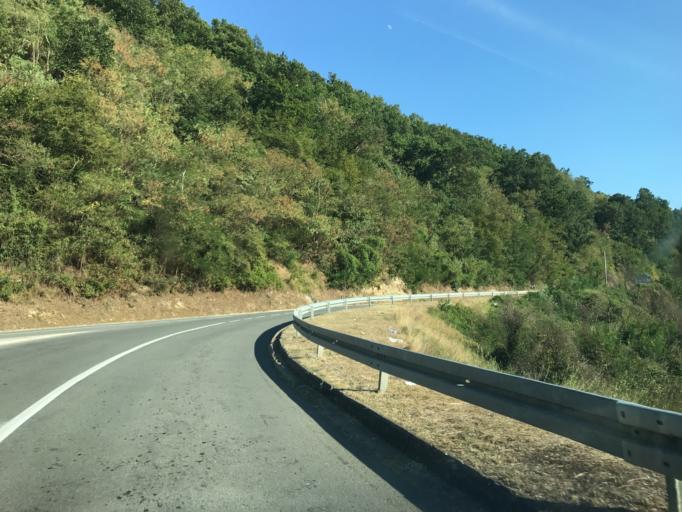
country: RO
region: Mehedinti
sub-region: Comuna Svinita
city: Svinita
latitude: 44.4467
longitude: 22.1759
